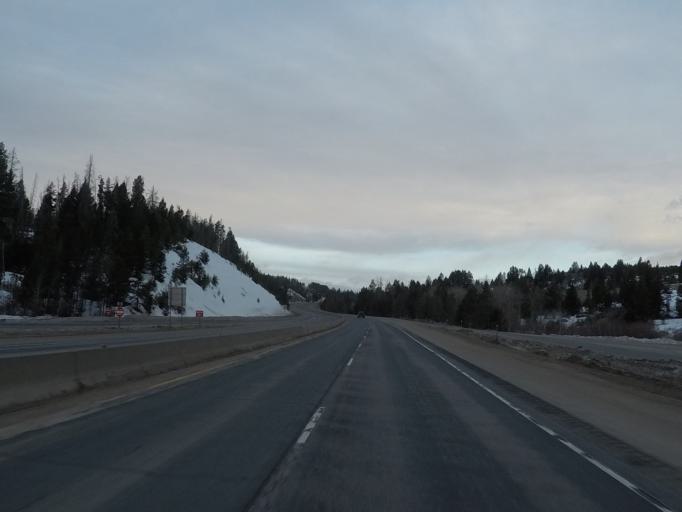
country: US
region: Montana
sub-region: Silver Bow County
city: Butte
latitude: 45.9153
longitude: -112.3781
